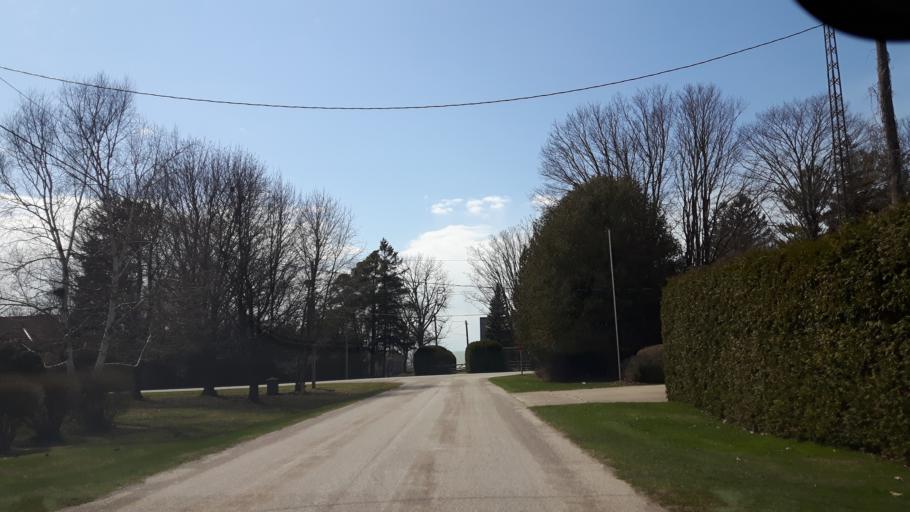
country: CA
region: Ontario
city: Bluewater
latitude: 43.5587
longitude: -81.7039
